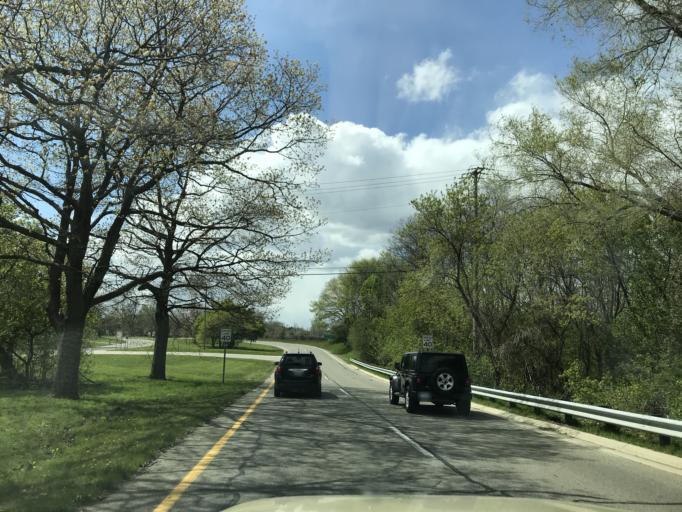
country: US
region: Michigan
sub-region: Wayne County
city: Plymouth
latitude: 42.3857
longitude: -83.4450
